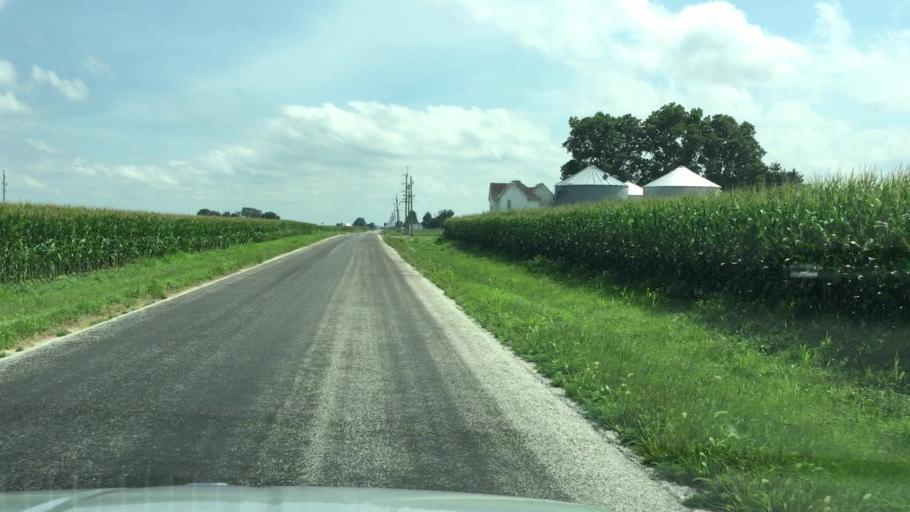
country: US
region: Illinois
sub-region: Hancock County
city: Carthage
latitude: 40.5227
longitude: -91.1771
